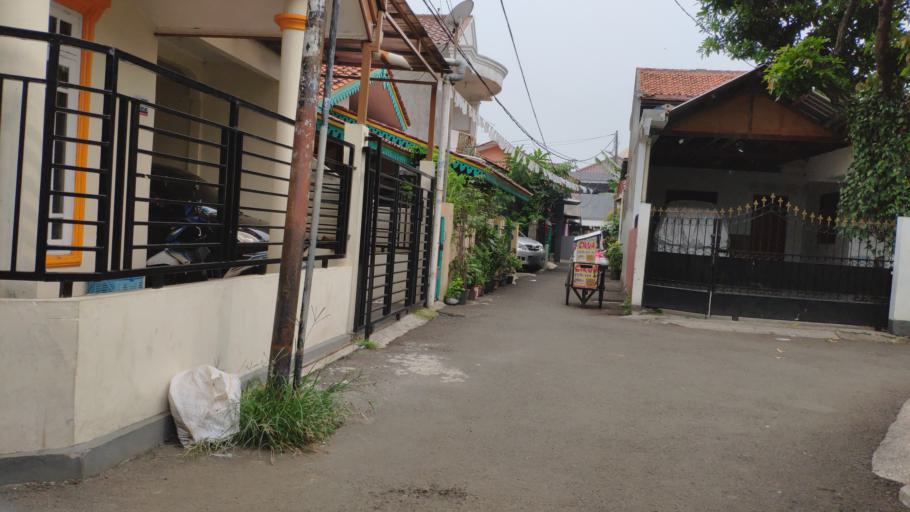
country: ID
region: West Java
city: Depok
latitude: -6.3511
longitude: 106.8006
